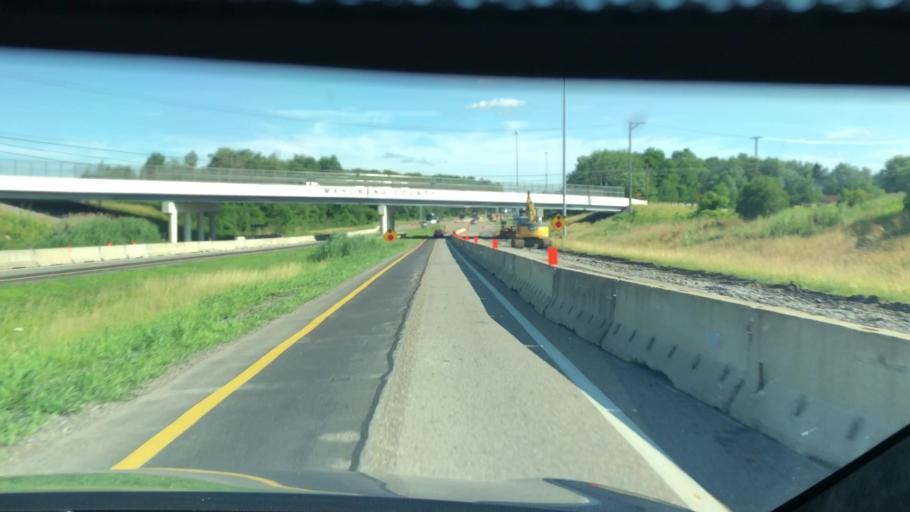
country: US
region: Ohio
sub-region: Mahoning County
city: Boardman
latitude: 40.9618
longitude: -80.6398
